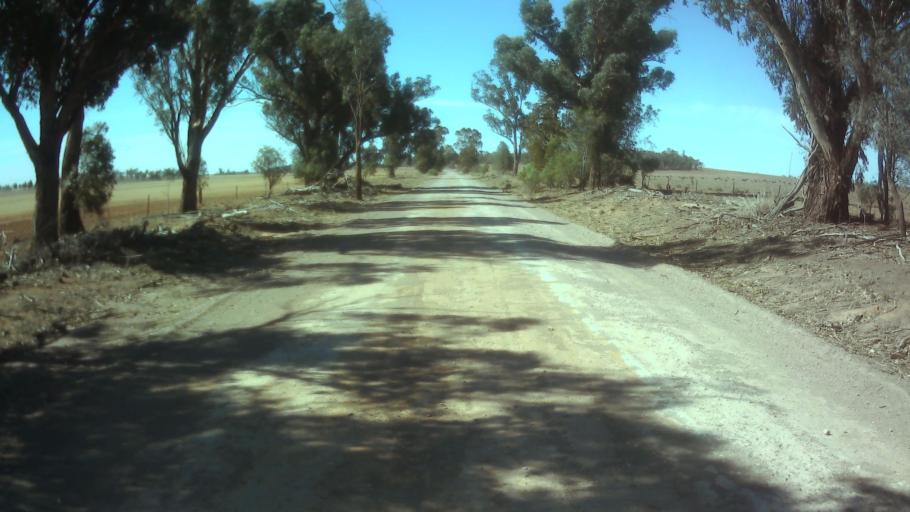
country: AU
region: New South Wales
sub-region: Forbes
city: Forbes
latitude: -33.7204
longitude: 147.7456
